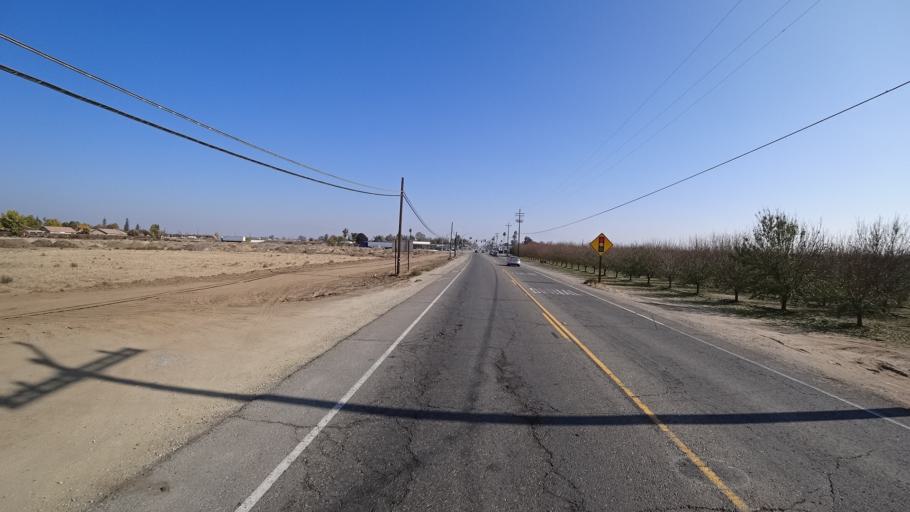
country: US
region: California
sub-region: Kern County
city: Greenfield
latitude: 35.2669
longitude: -119.0411
